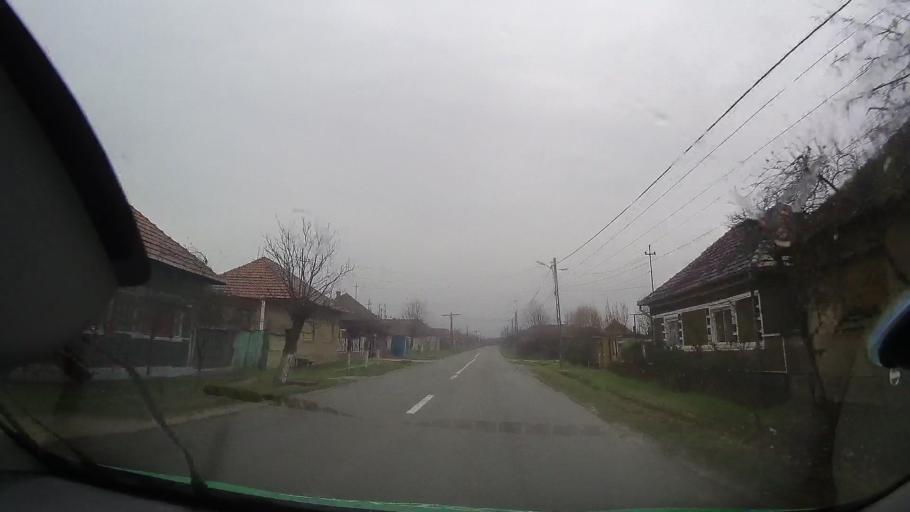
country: RO
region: Bihor
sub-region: Comuna Tinca
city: Gurbediu
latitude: 46.7849
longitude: 21.8673
